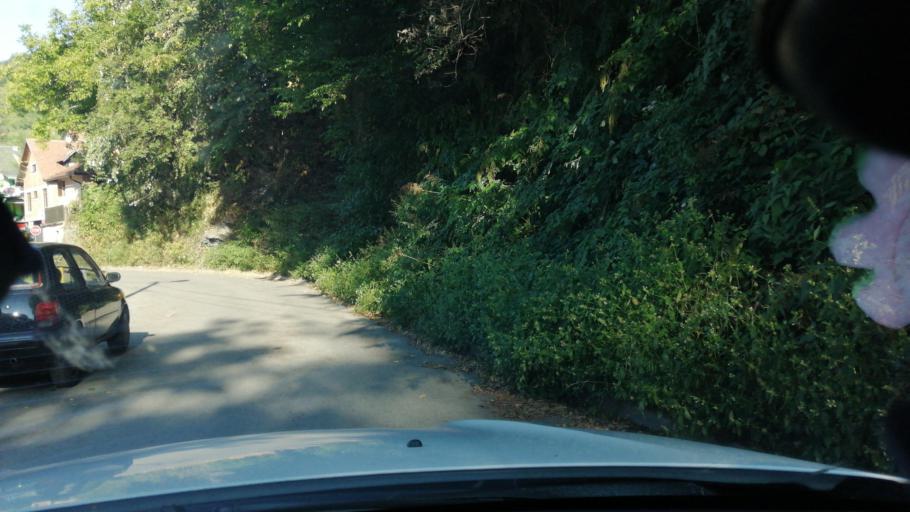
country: RS
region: Central Serbia
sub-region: Moravicki Okrug
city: Ivanjica
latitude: 43.5851
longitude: 20.2237
